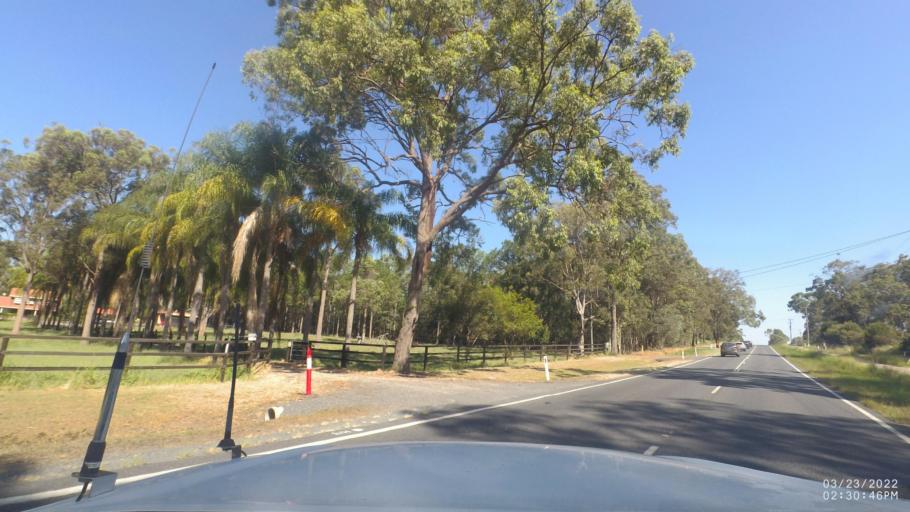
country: AU
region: Queensland
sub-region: Logan
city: Logan Reserve
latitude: -27.7388
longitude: 153.1257
